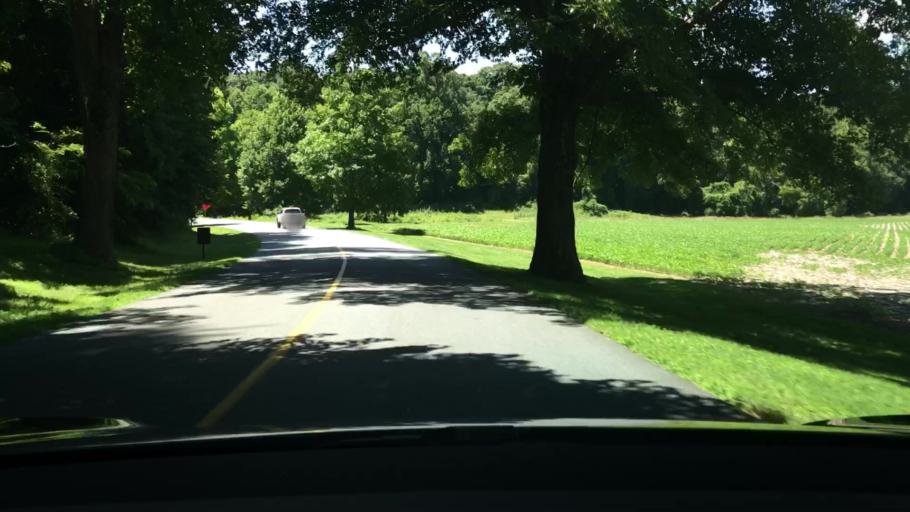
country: US
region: North Carolina
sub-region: Buncombe County
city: Asheville
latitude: 35.5640
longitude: -82.5704
